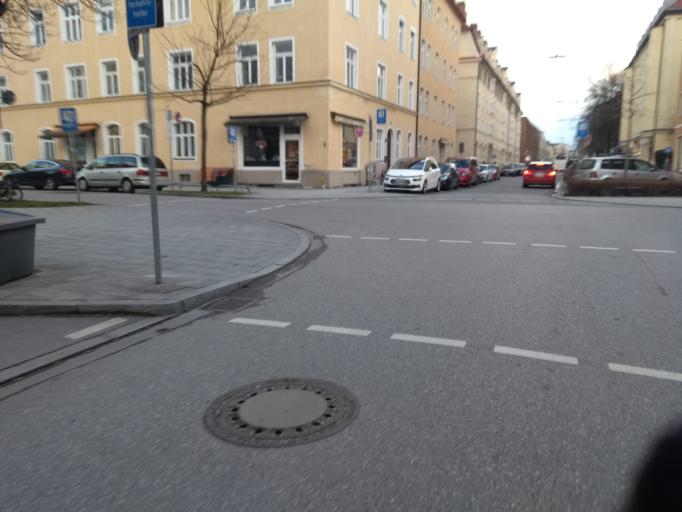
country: DE
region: Bavaria
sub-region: Upper Bavaria
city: Munich
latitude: 48.1373
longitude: 11.5374
